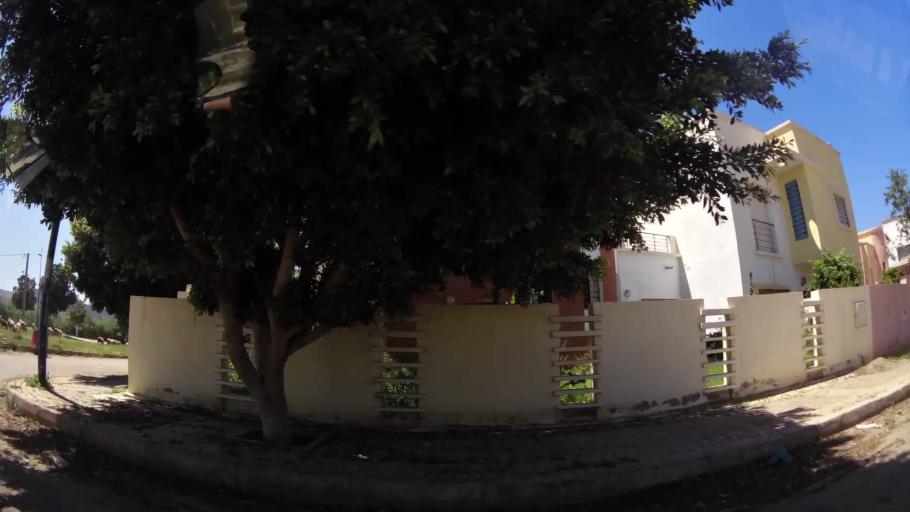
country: MA
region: Oriental
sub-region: Berkane-Taourirt
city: Madagh
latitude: 35.0714
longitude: -2.2172
